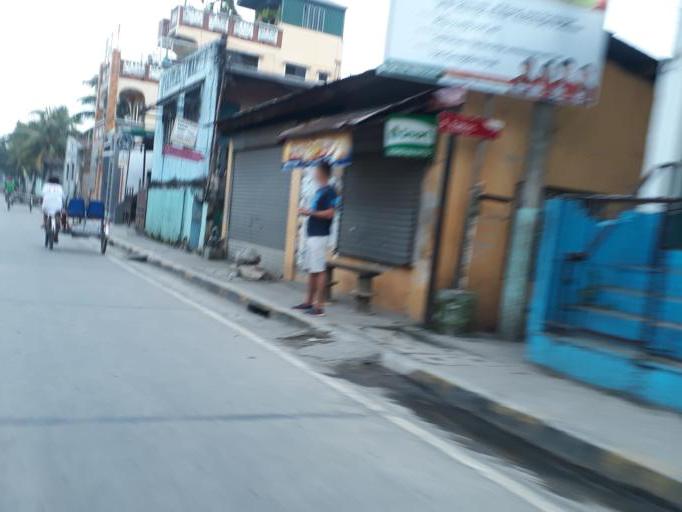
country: PH
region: Central Luzon
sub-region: Province of Bulacan
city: Obando
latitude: 14.7025
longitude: 120.9494
